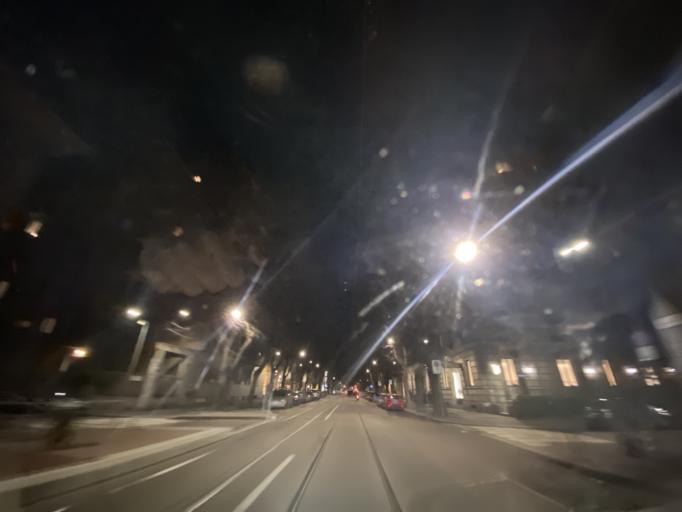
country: IT
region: Lombardy
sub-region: Citta metropolitana di Milano
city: Milano
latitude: 45.4704
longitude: 9.1699
